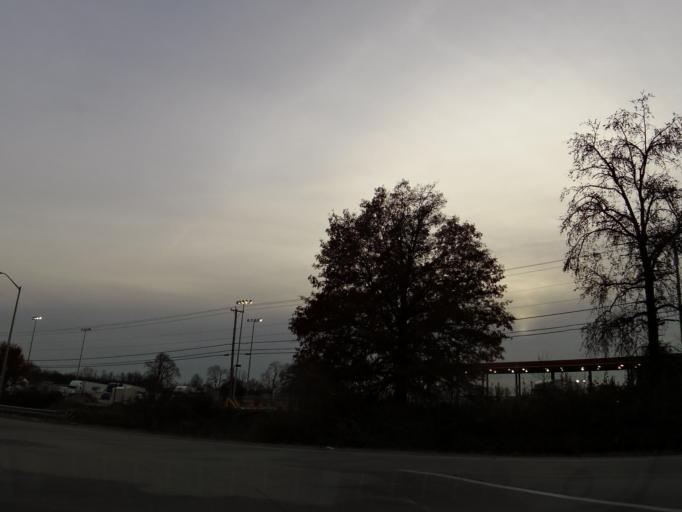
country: US
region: Kentucky
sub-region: Scott County
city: Georgetown
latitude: 38.2767
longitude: -84.5588
